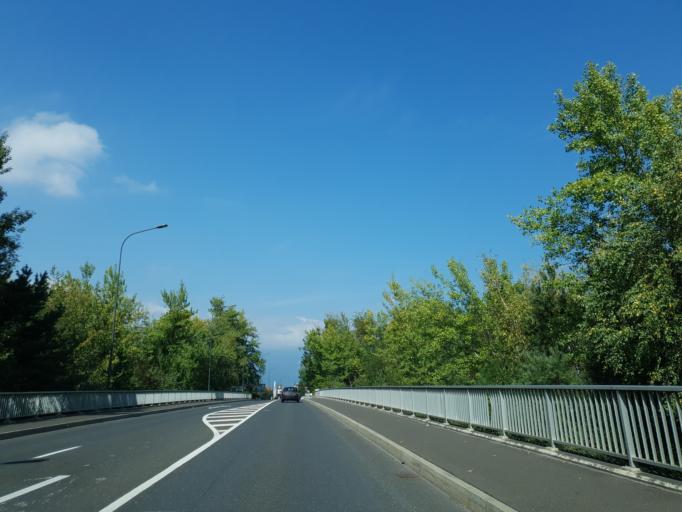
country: LI
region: Schaan
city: Schaan
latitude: 47.1528
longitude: 9.5109
